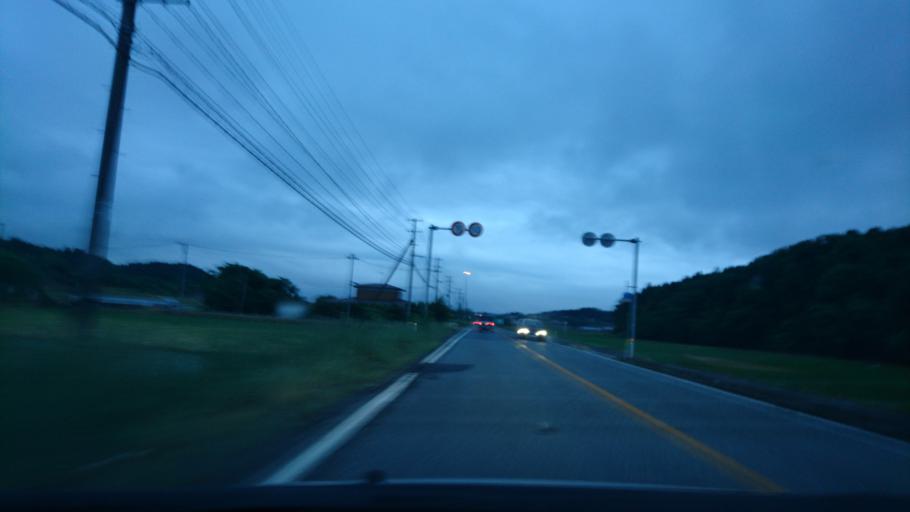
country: JP
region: Iwate
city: Ichinoseki
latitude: 38.8232
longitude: 141.0792
